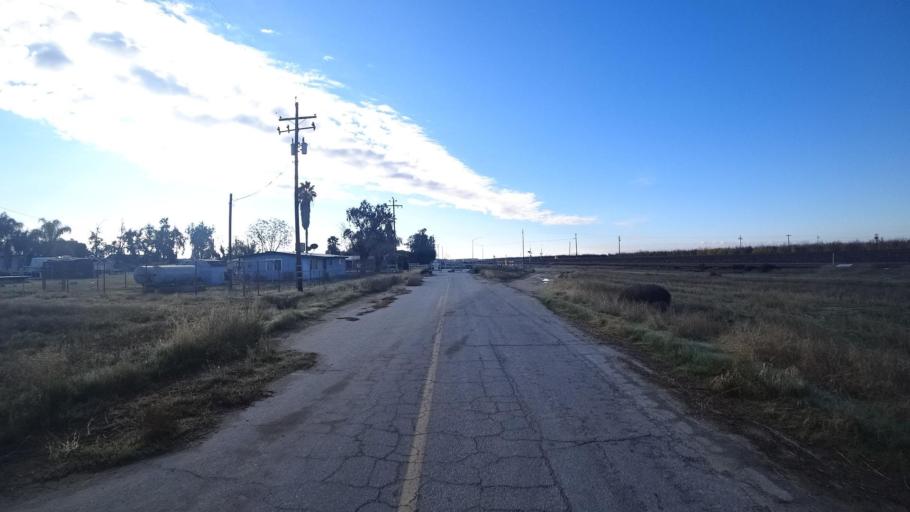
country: US
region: California
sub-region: Kern County
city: Delano
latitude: 35.7192
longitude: -119.3303
